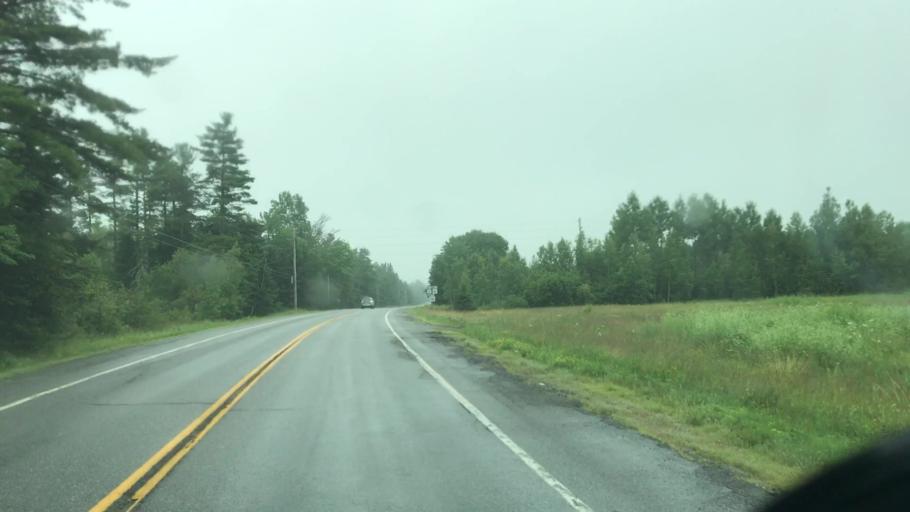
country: US
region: Maine
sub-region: Penobscot County
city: Howland
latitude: 45.2519
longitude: -68.6378
